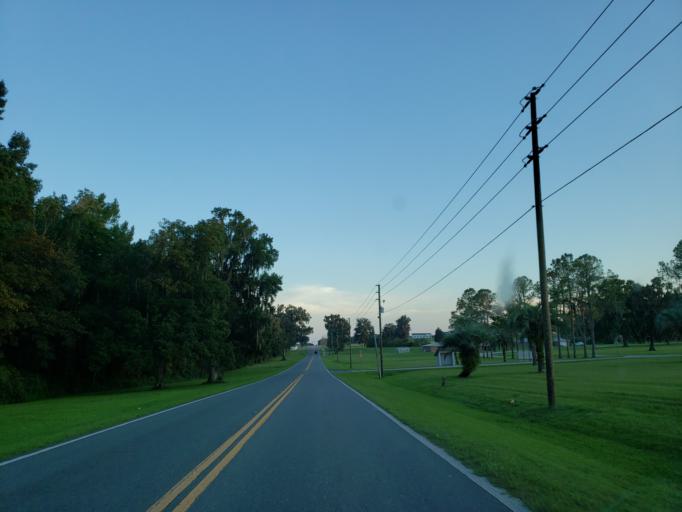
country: US
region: Florida
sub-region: Marion County
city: Citra
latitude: 29.3173
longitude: -82.1958
